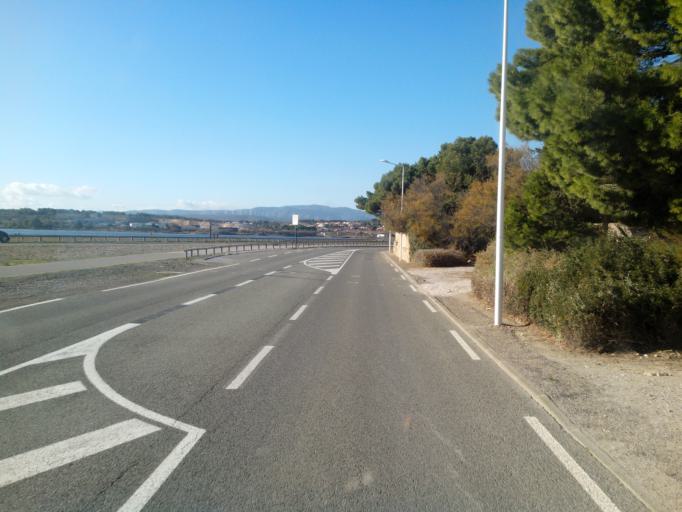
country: FR
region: Languedoc-Roussillon
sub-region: Departement de l'Aude
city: Leucate
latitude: 42.9039
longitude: 3.0482
